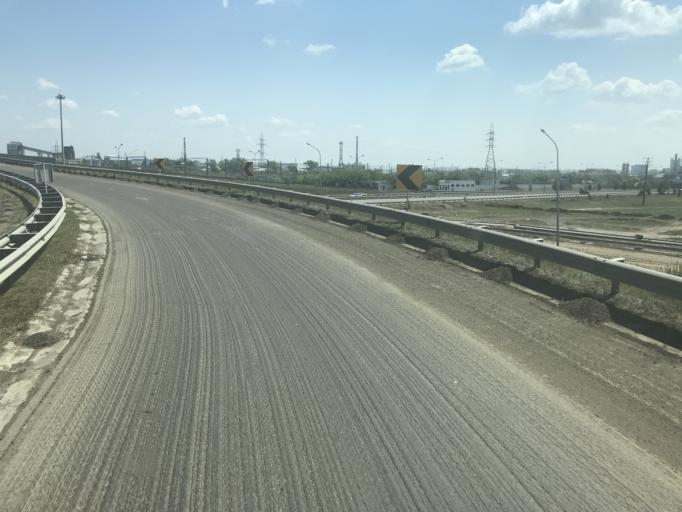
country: KZ
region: Aqmola
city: Kokshetau
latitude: 53.3175
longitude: 69.3951
